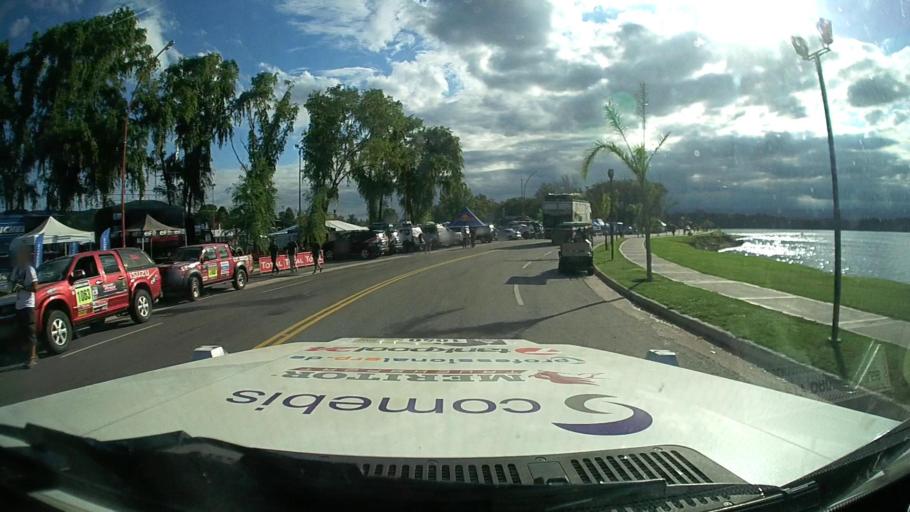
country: AR
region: Cordoba
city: Villa Carlos Paz
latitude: -31.3981
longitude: -64.4797
